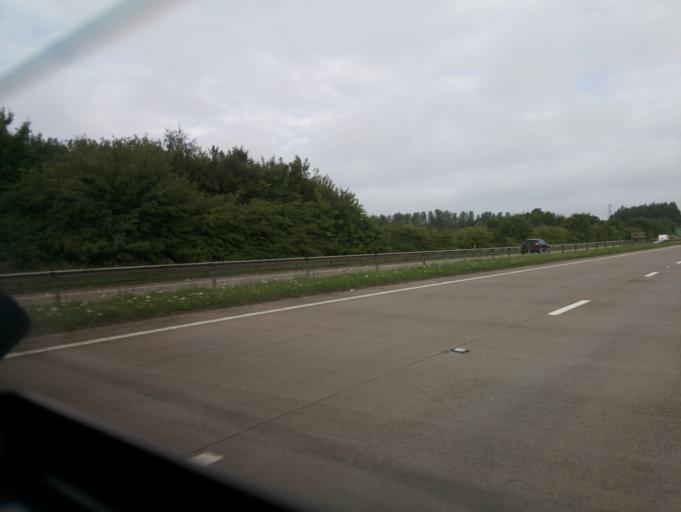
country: GB
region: England
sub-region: Gloucestershire
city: Cirencester
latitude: 51.7166
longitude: -1.9376
